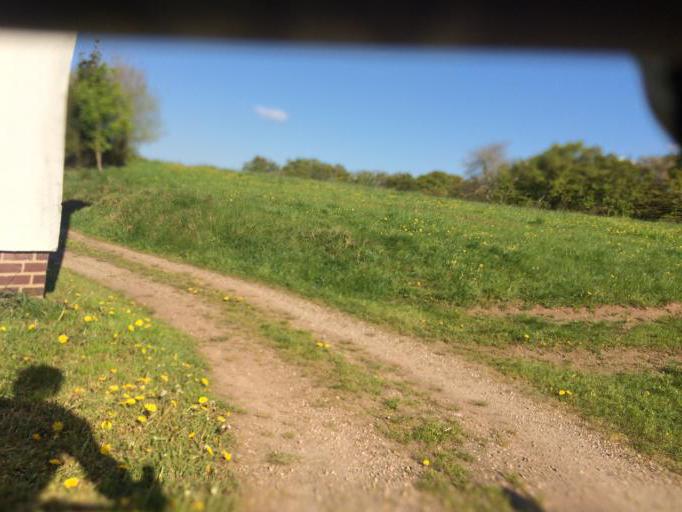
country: DE
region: Hesse
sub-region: Regierungsbezirk Kassel
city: Korbach
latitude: 51.1695
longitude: 8.8382
